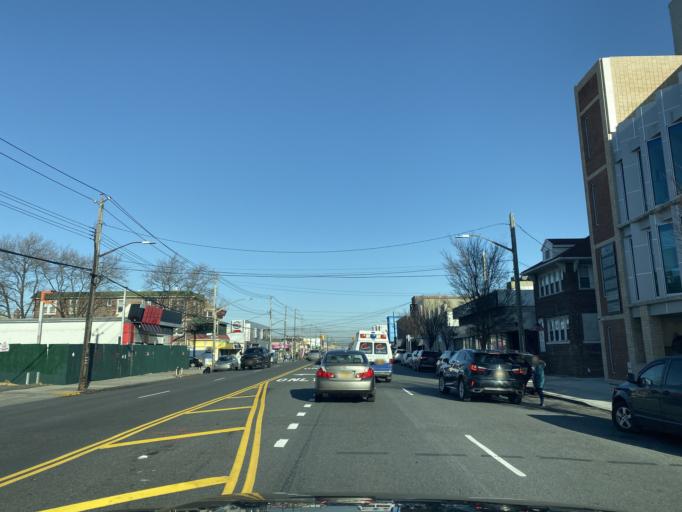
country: US
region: New York
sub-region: Kings County
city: Coney Island
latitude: 40.5881
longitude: -73.9604
